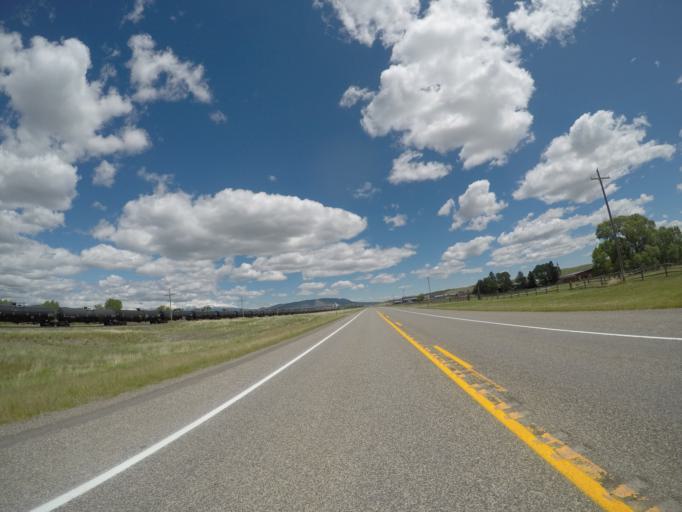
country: US
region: Montana
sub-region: Park County
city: Livingston
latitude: 45.6819
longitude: -110.5190
